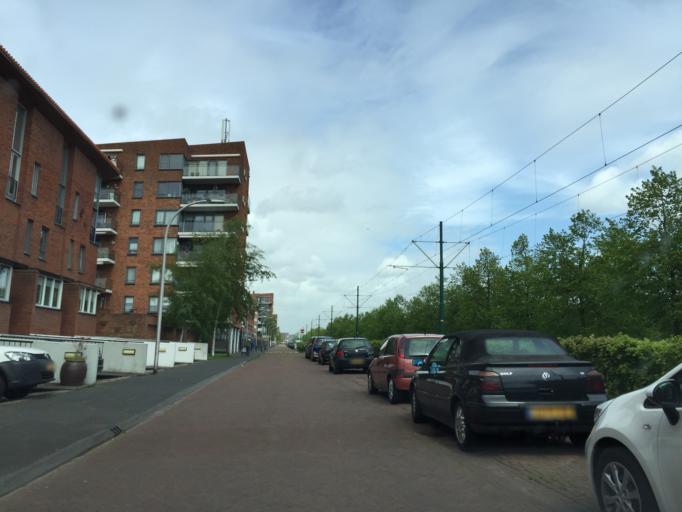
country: NL
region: South Holland
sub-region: Gemeente Den Haag
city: Ypenburg
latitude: 52.0361
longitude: 4.3639
